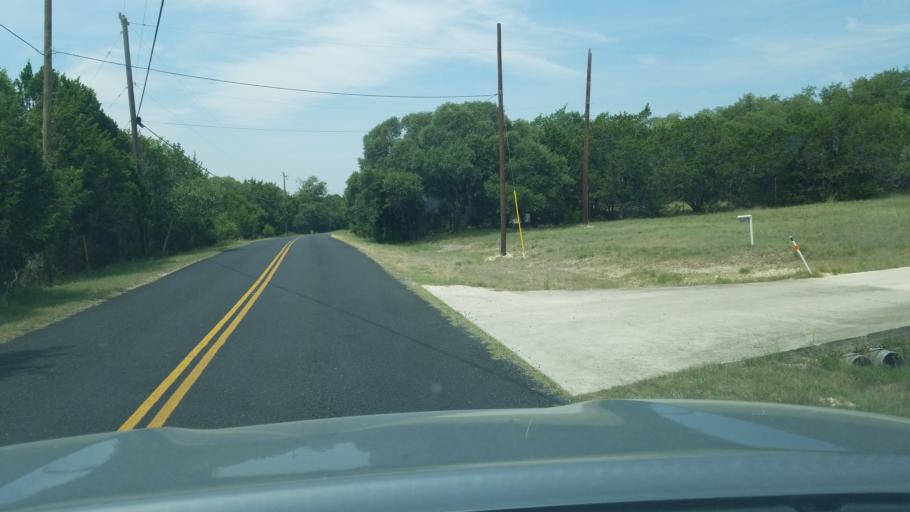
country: US
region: Texas
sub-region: Comal County
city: Bulverde
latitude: 29.7744
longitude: -98.4446
